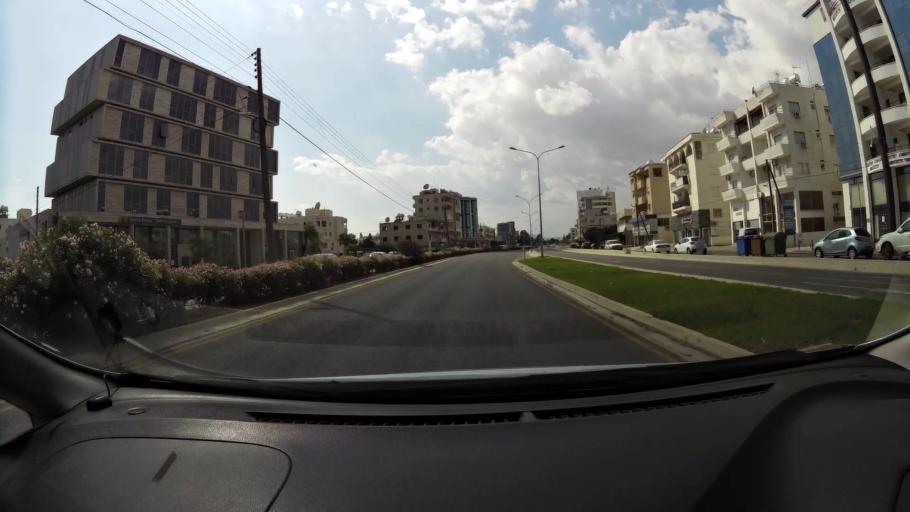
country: CY
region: Larnaka
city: Larnaca
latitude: 34.9177
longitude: 33.6119
